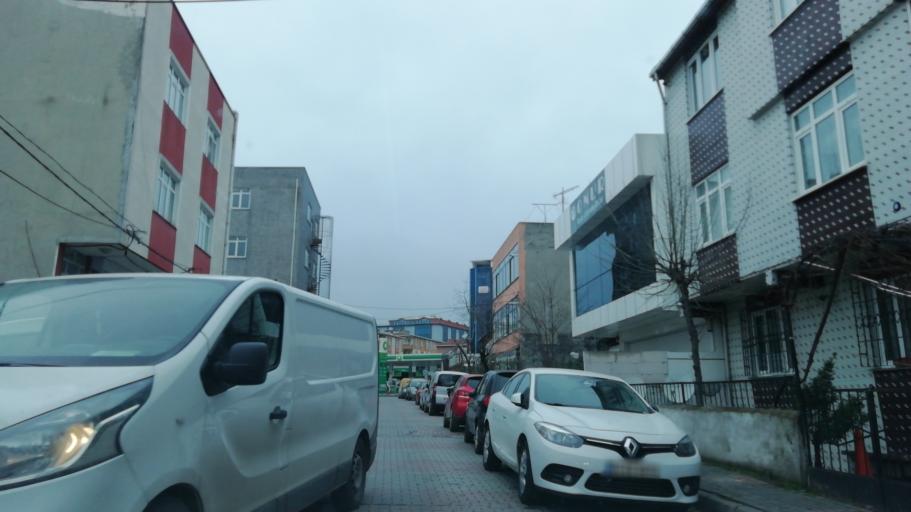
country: TR
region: Istanbul
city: Bahcelievler
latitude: 41.0132
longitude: 28.8269
